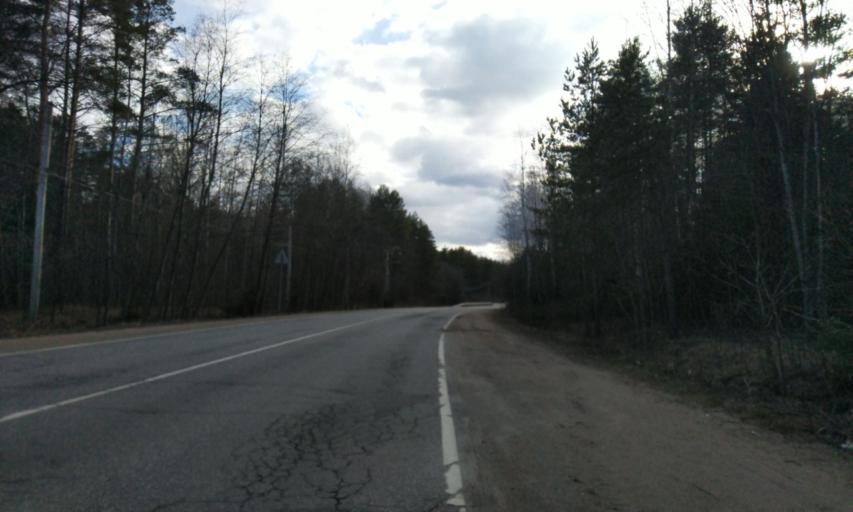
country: RU
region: Leningrad
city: Toksovo
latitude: 60.1261
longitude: 30.4622
